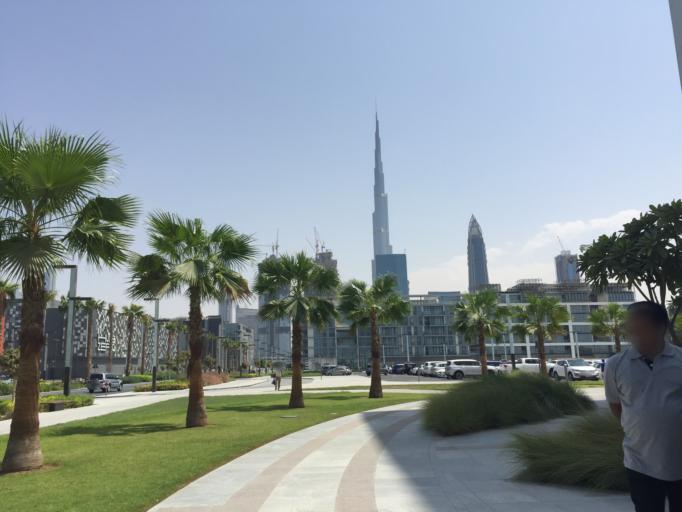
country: AE
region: Dubai
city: Dubai
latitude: 25.2065
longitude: 55.2605
